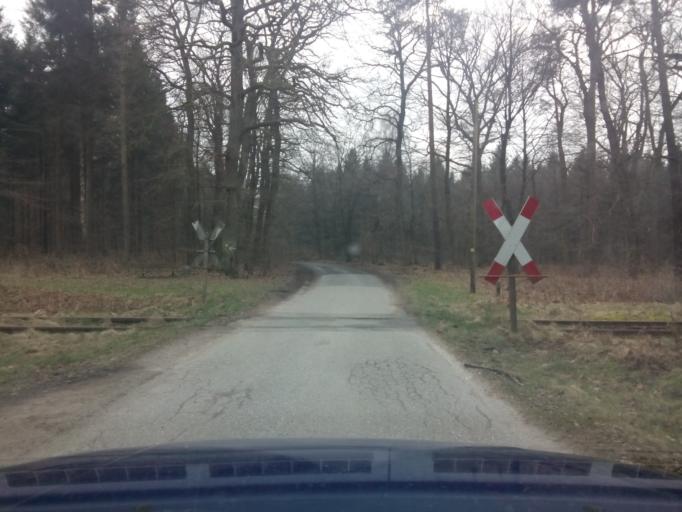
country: DE
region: Lower Saxony
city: Drangstedt
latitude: 53.6169
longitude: 8.7261
